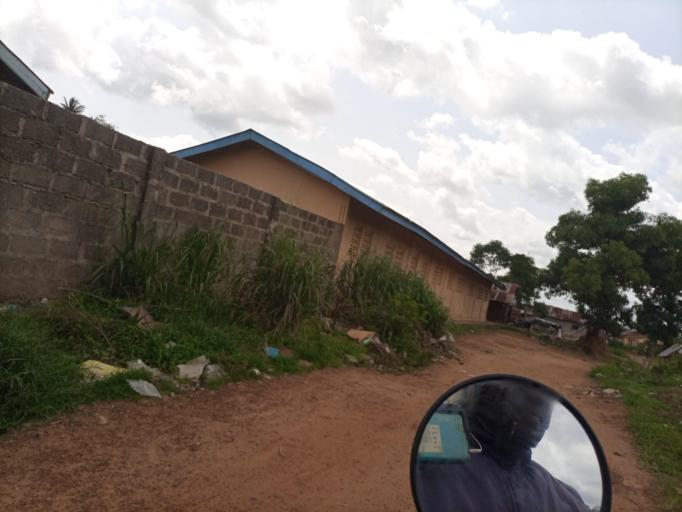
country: SL
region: Southern Province
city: Bo
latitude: 7.9505
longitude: -11.7320
